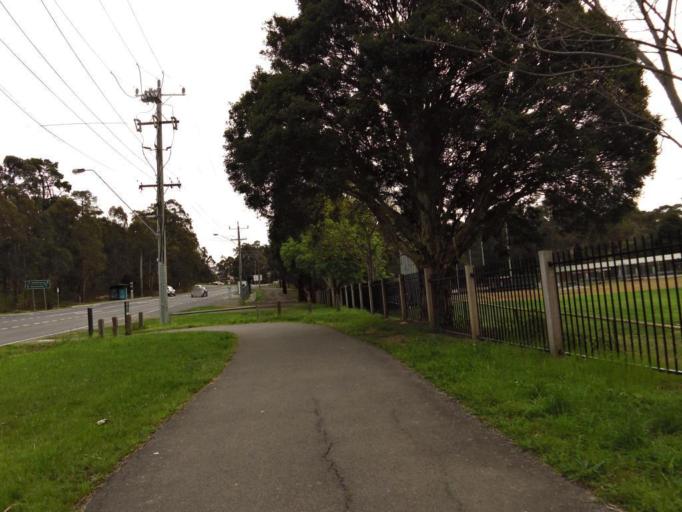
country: AU
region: Victoria
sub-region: Nillumbik
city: Eltham
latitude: -37.7512
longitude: 145.1757
